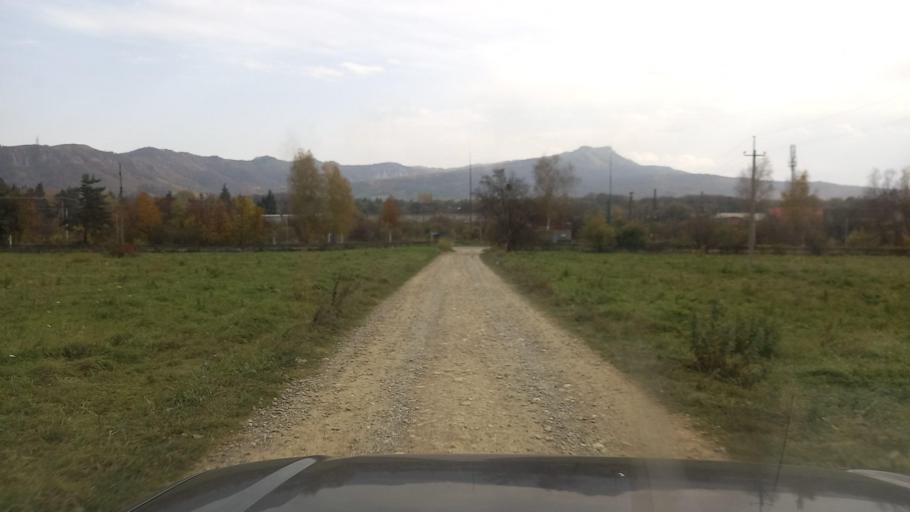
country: RU
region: Krasnodarskiy
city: Psebay
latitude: 44.1484
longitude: 40.8266
